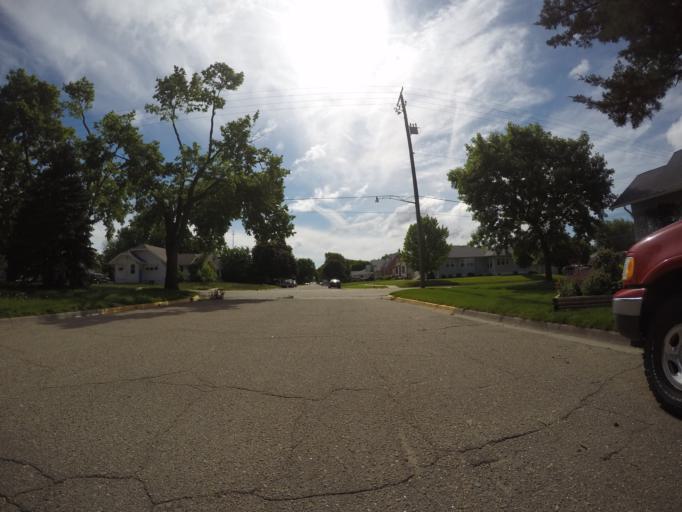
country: US
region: Nebraska
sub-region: Buffalo County
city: Kearney
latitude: 40.7037
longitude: -99.0929
